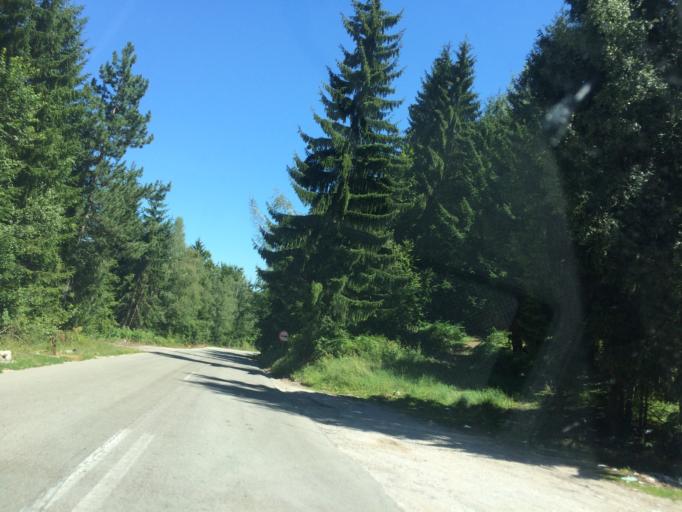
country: RS
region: Central Serbia
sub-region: Zlatiborski Okrug
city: Prijepolje
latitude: 43.3310
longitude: 19.5351
